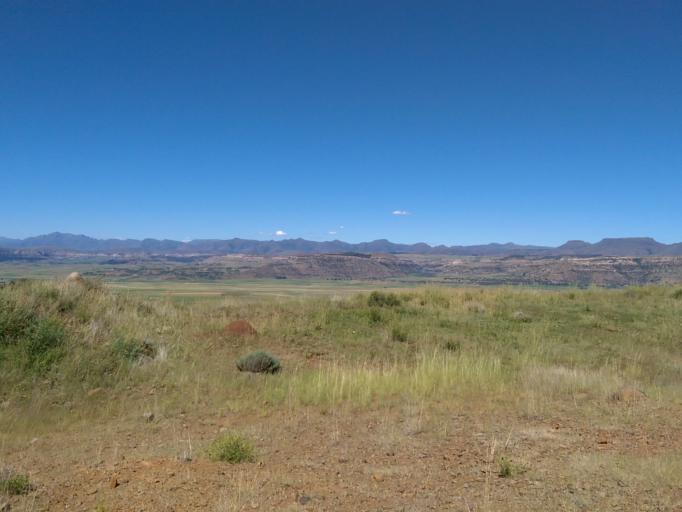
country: LS
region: Maseru
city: Maseru
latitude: -29.4857
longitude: 27.5822
